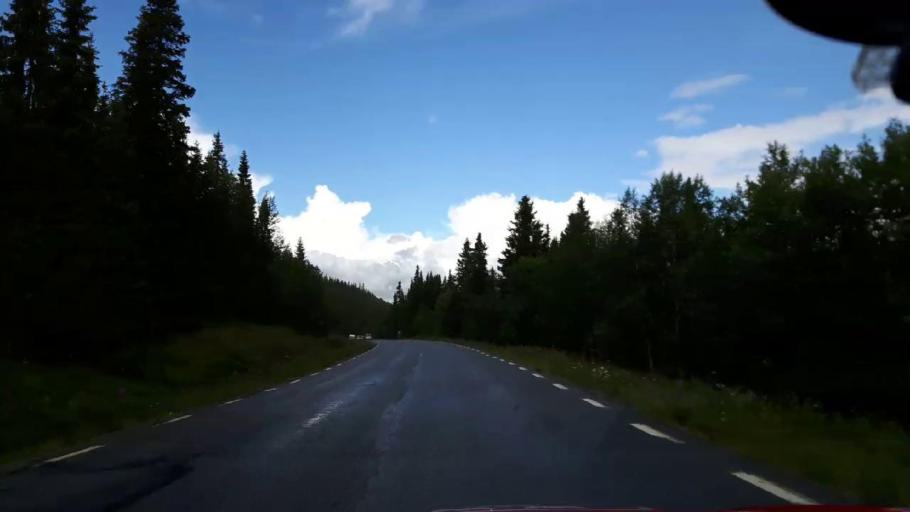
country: SE
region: Vaesterbotten
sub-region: Vilhelmina Kommun
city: Sjoberg
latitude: 65.0216
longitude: 15.1613
